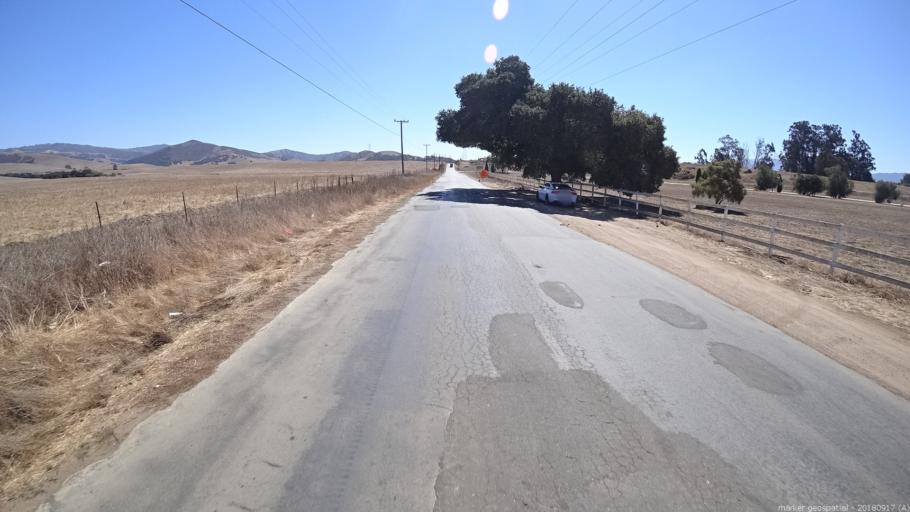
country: US
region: California
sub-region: Monterey County
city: Salinas
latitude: 36.7049
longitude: -121.5800
